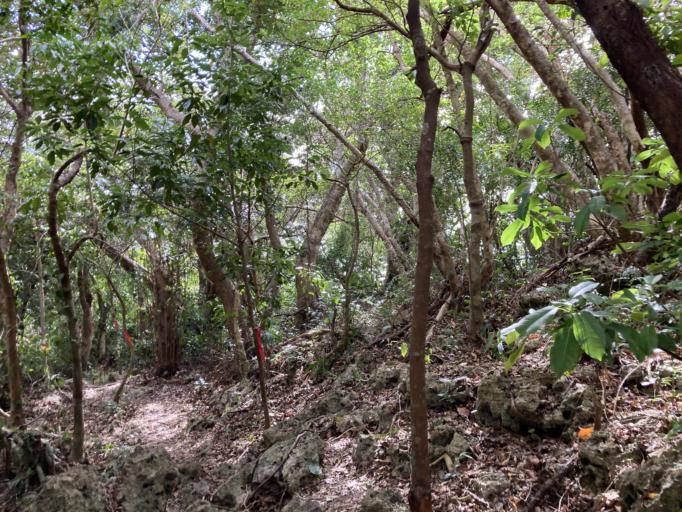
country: JP
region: Okinawa
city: Tomigusuku
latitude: 26.1423
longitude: 127.7832
